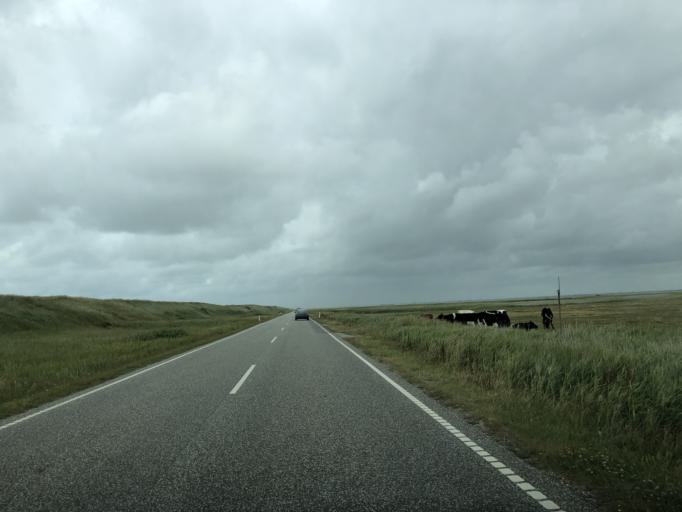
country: DK
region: Central Jutland
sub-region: Lemvig Kommune
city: Harboore
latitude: 56.3975
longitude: 8.1215
